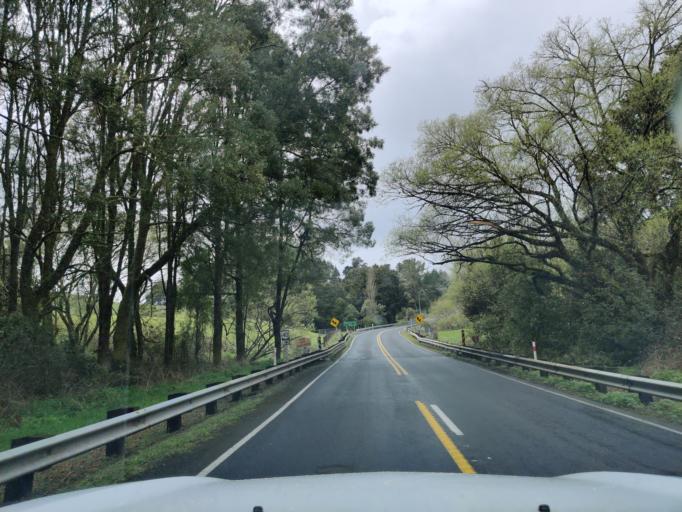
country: NZ
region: Waikato
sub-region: Otorohanga District
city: Otorohanga
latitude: -38.6966
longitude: 175.2255
